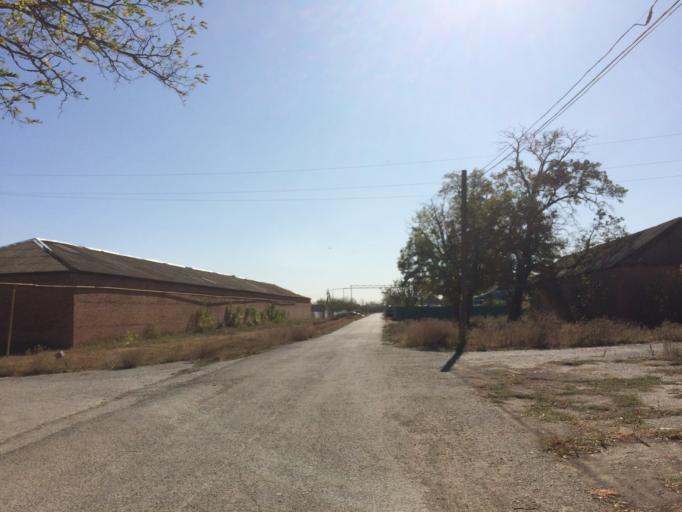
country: RU
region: Rostov
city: Gigant
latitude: 46.5156
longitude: 41.1888
